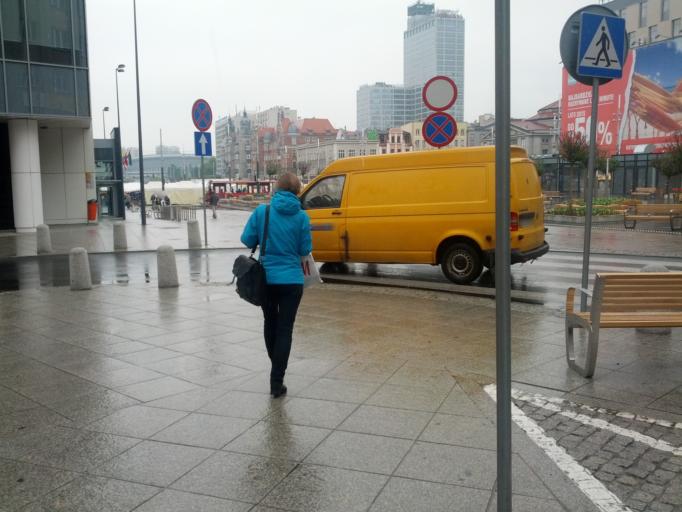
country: PL
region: Silesian Voivodeship
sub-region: Katowice
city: Katowice
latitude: 50.2587
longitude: 19.0211
